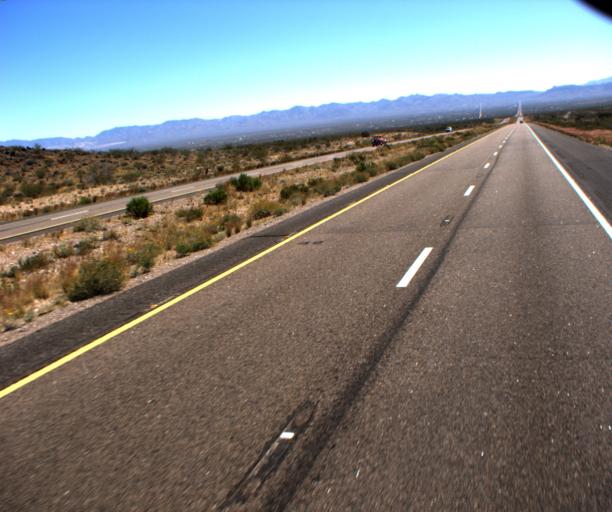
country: US
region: Arizona
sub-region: Mohave County
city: Golden Valley
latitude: 35.2286
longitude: -114.3561
